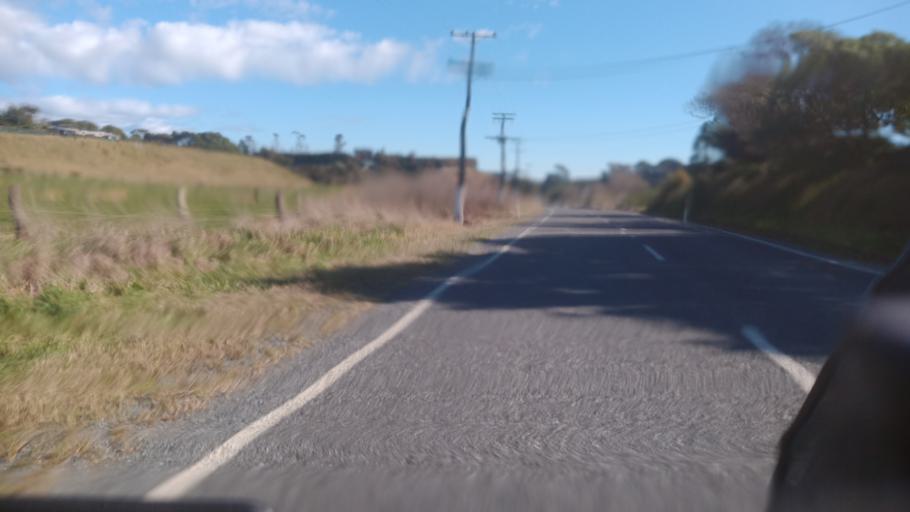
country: NZ
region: Bay of Plenty
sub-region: Opotiki District
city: Opotiki
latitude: -37.9879
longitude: 177.3568
